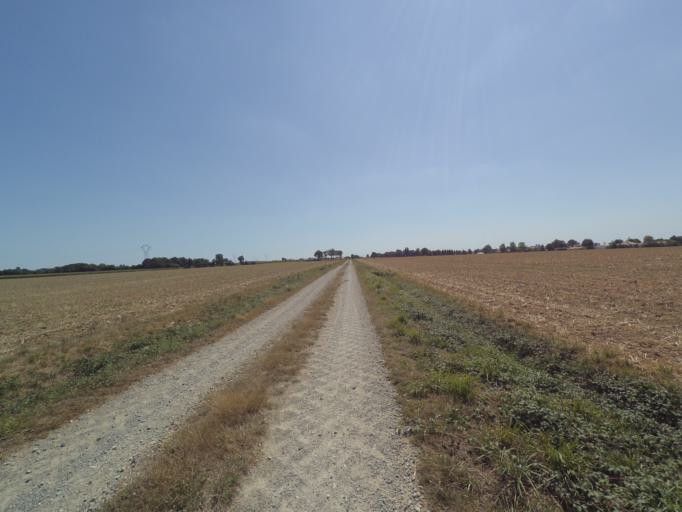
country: FR
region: Pays de la Loire
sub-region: Departement de la Loire-Atlantique
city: La Planche
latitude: 46.9961
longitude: -1.4136
